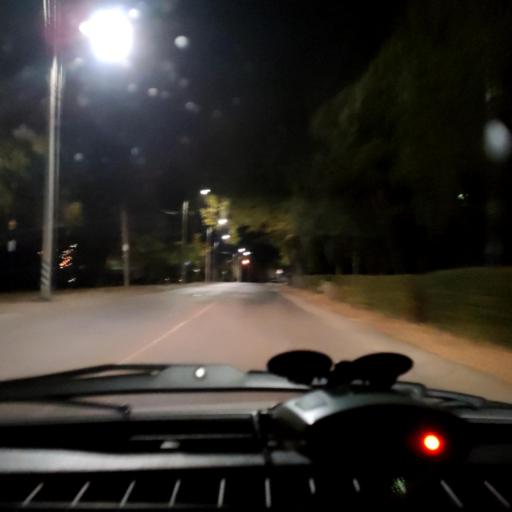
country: RU
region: Voronezj
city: Semiluki
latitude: 51.6792
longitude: 39.0300
